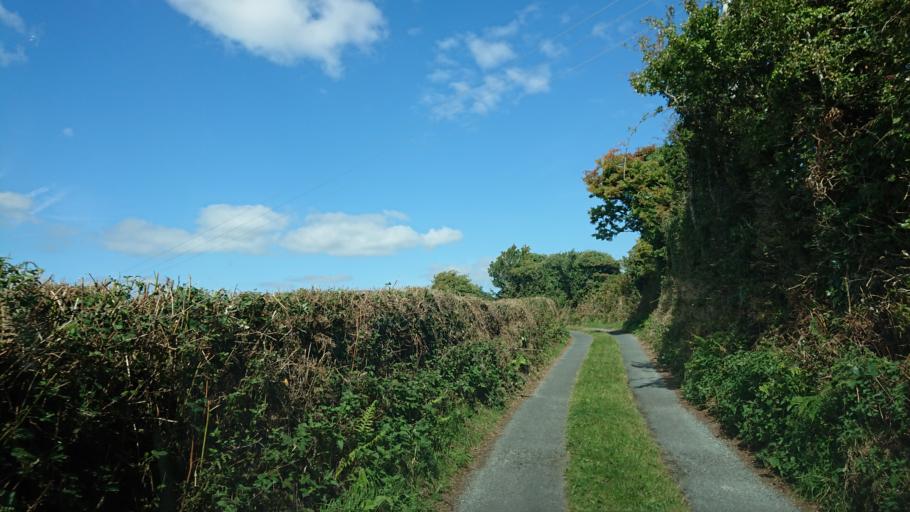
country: IE
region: Munster
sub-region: Waterford
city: Waterford
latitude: 52.2317
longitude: -7.1560
